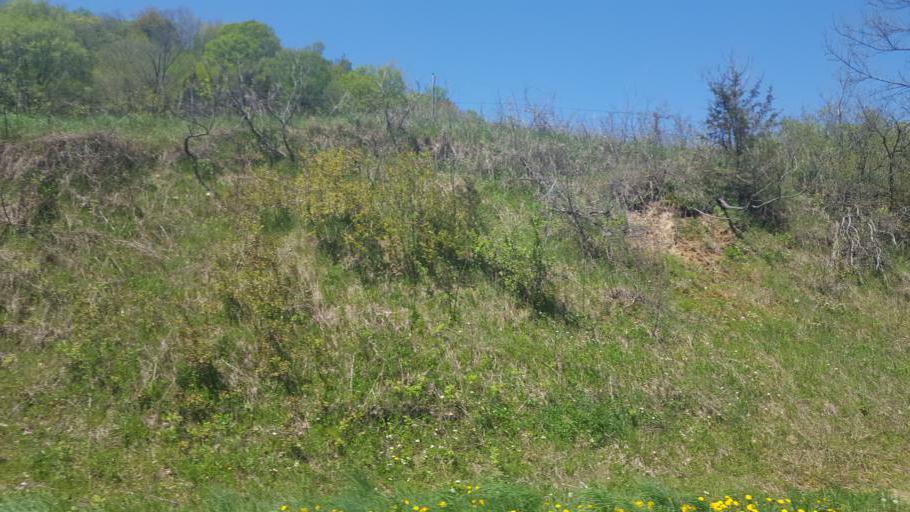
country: US
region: Wisconsin
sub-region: Vernon County
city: Hillsboro
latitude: 43.5850
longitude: -90.4399
